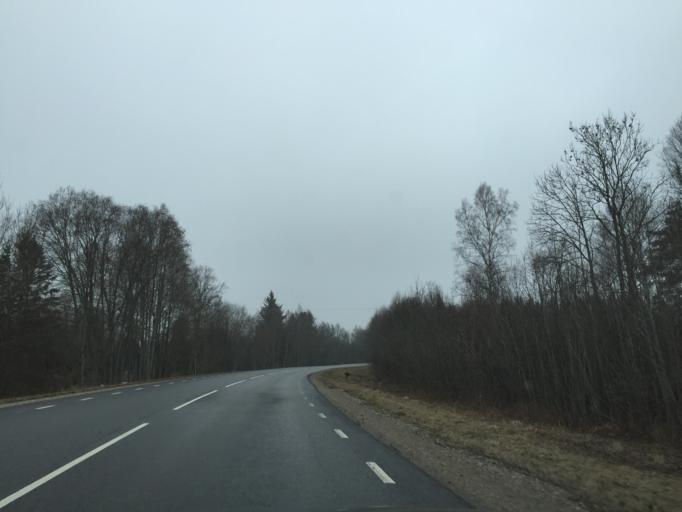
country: EE
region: Laeaene
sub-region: Lihula vald
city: Lihula
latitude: 58.5953
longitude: 23.7042
